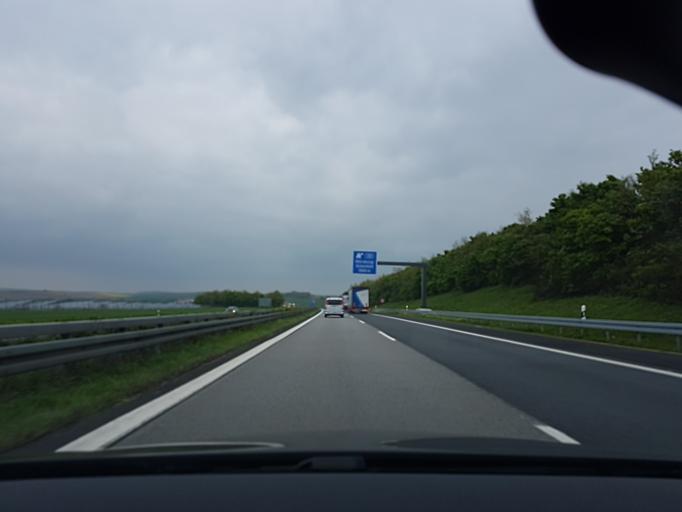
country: DE
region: Bavaria
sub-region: Regierungsbezirk Unterfranken
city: Kurnach
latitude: 49.8367
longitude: 10.0324
